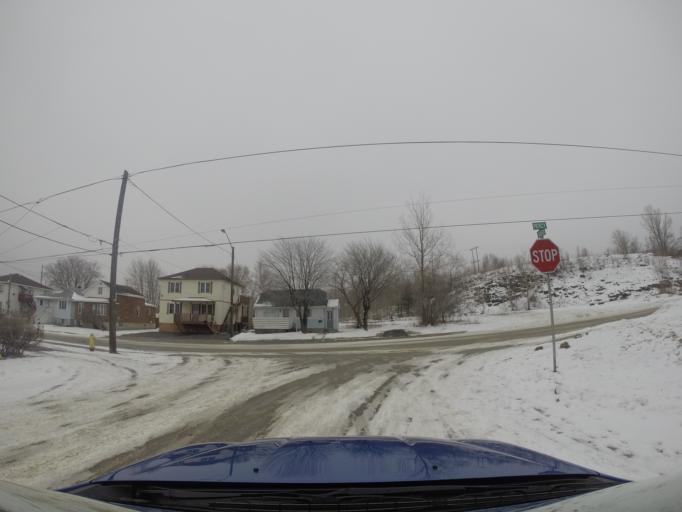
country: CA
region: Ontario
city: Greater Sudbury
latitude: 46.5035
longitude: -80.9821
